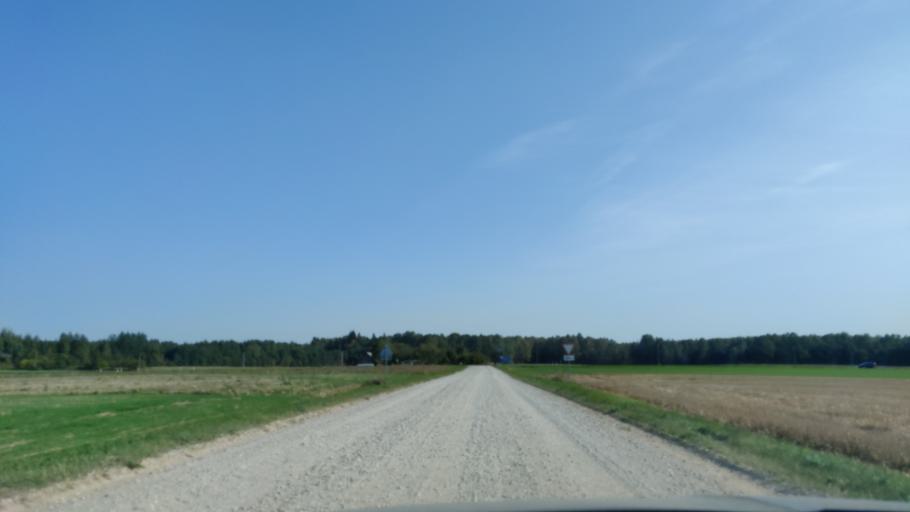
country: LT
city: Sirvintos
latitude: 54.9662
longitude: 24.8563
